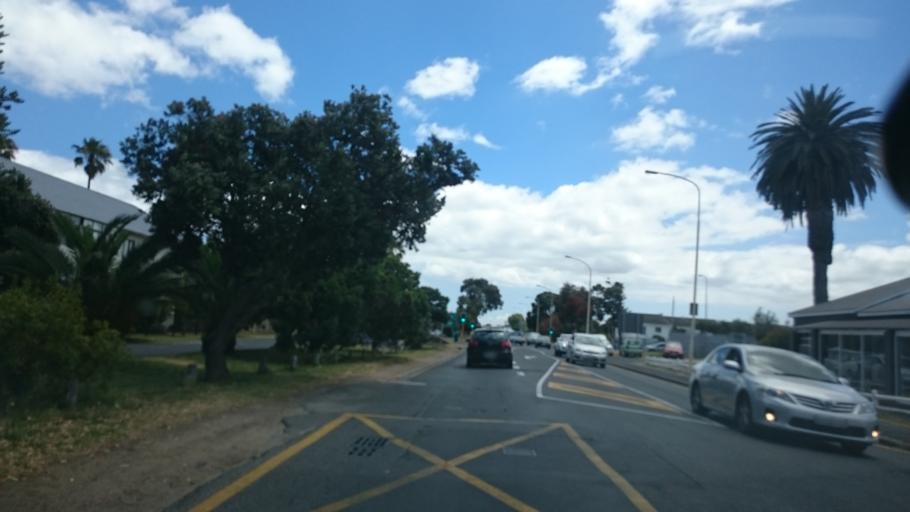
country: ZA
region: Western Cape
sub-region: City of Cape Town
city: Bergvliet
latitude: -34.0433
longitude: 18.4635
